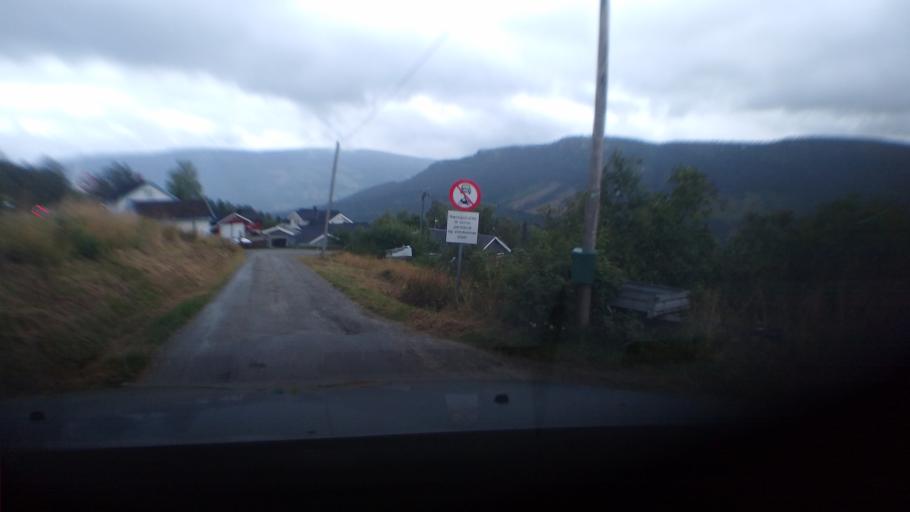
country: NO
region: Oppland
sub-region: Ringebu
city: Ringebu
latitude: 61.5951
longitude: 10.0510
